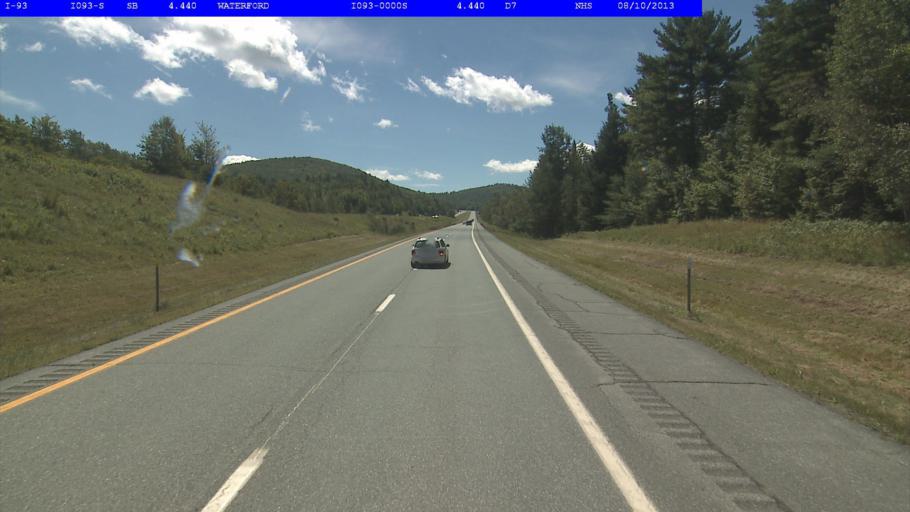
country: US
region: Vermont
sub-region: Caledonia County
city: Saint Johnsbury
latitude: 44.3996
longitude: -71.9197
